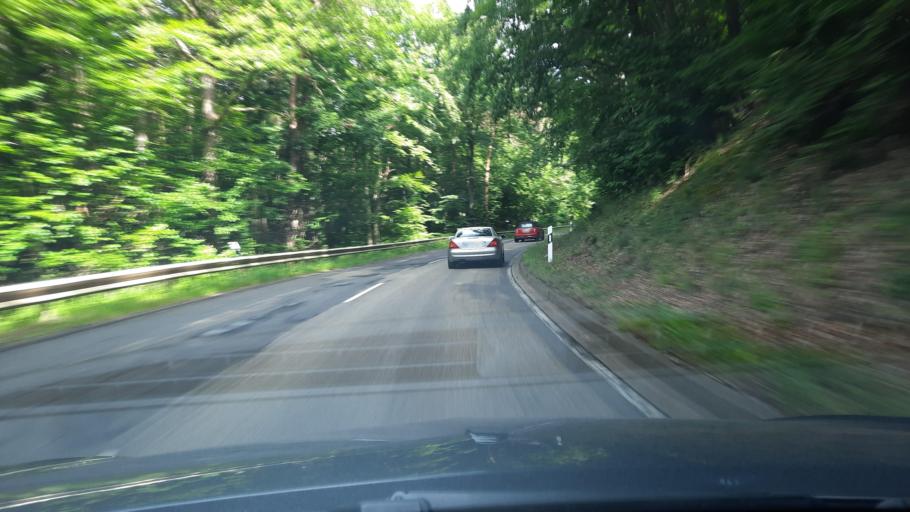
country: DE
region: Rheinland-Pfalz
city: Spessart
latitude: 50.4439
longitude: 7.1319
